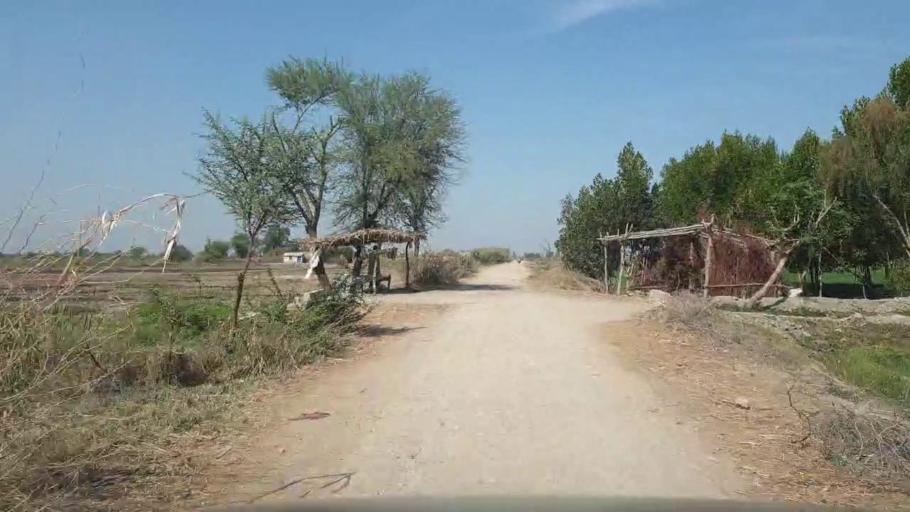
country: PK
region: Sindh
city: Mirpur Khas
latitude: 25.4405
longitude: 69.1642
